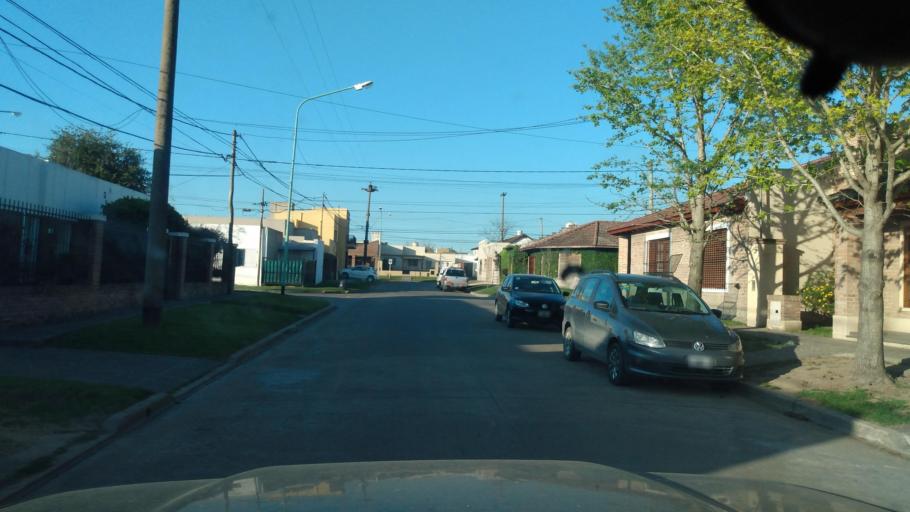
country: AR
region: Buenos Aires
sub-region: Partido de Lujan
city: Lujan
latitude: -34.5777
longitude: -59.1127
